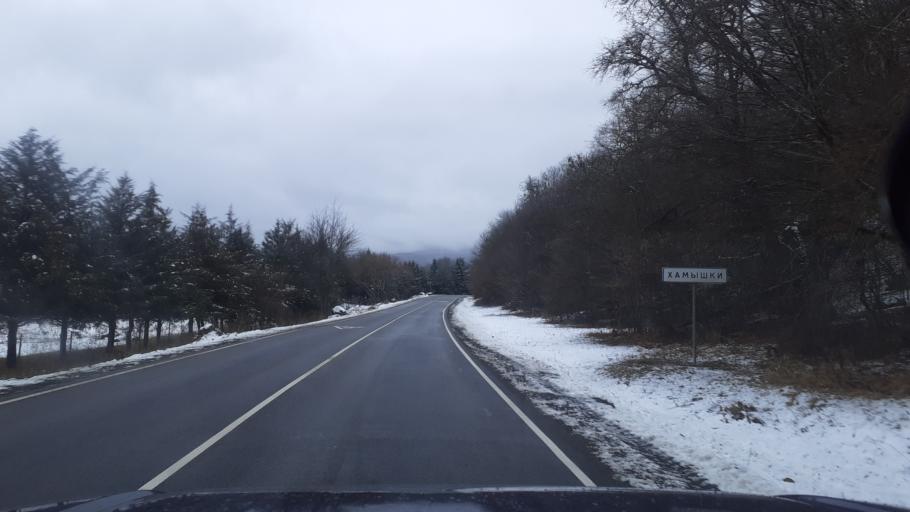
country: RU
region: Adygeya
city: Kamennomostskiy
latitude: 44.1166
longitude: 40.1209
